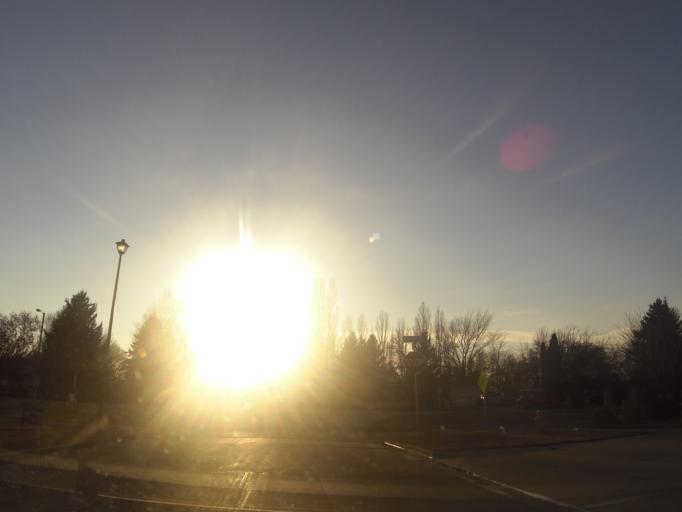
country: US
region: North Dakota
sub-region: Grand Forks County
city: Grand Forks
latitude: 47.8698
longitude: -97.0285
